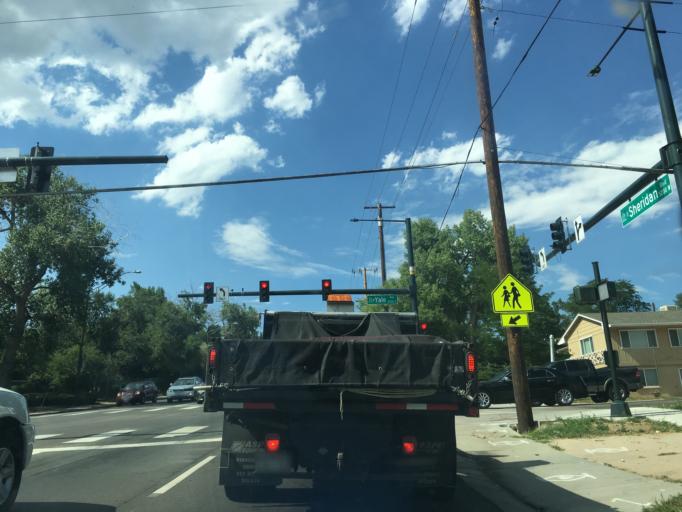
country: US
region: Colorado
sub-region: Arapahoe County
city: Sheridan
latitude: 39.6675
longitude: -105.0532
